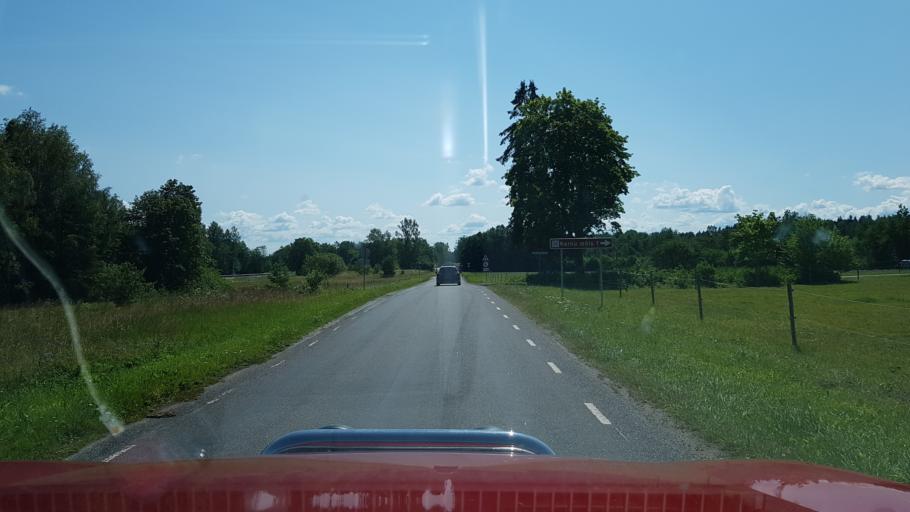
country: EE
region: Harju
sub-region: Saue linn
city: Saue
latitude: 59.1633
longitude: 24.5020
